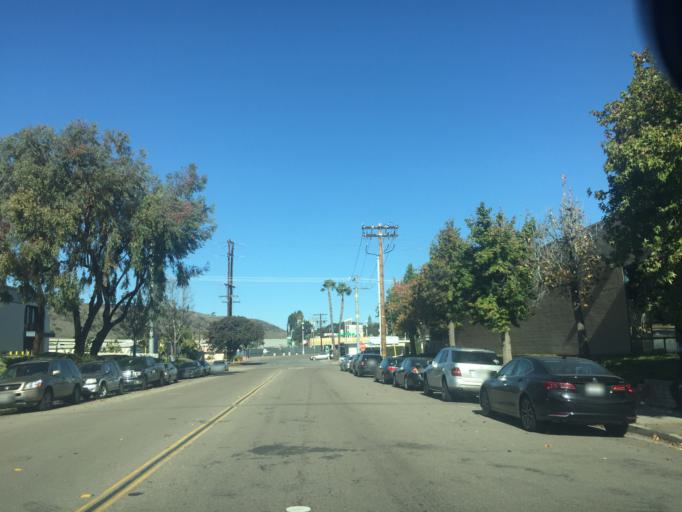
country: US
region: California
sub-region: San Diego County
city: La Mesa
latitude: 32.7869
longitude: -117.1015
